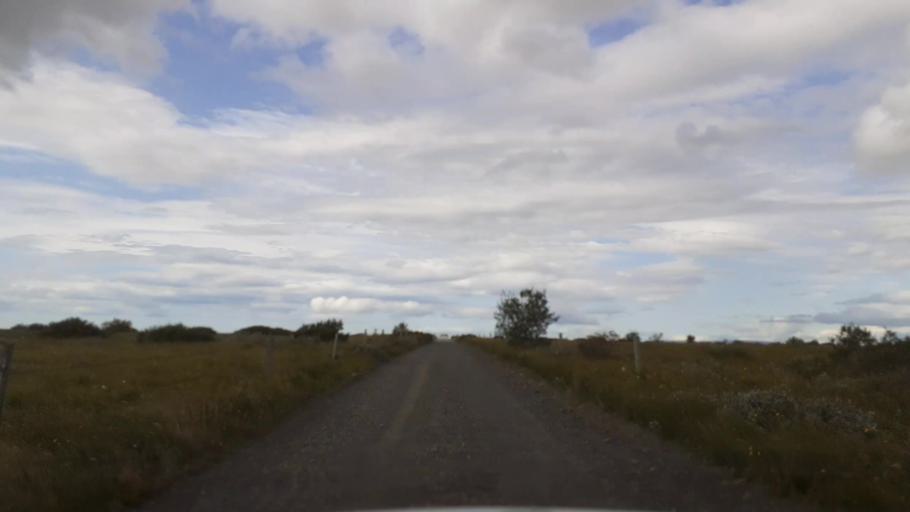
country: IS
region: South
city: Vestmannaeyjar
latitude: 63.8191
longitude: -20.4232
